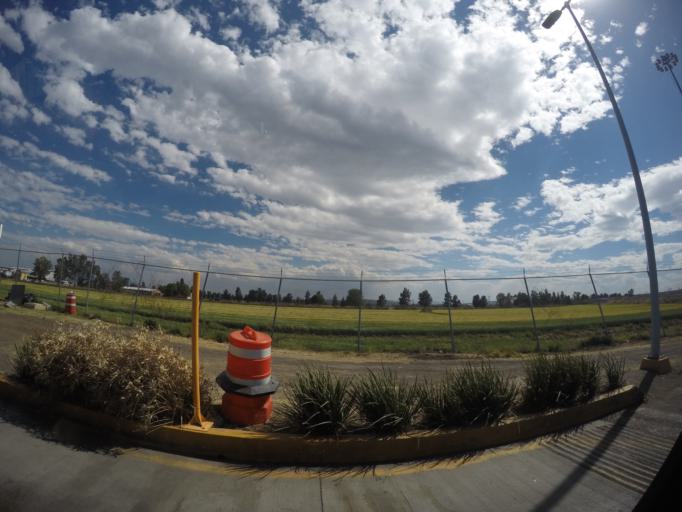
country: MX
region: Guanajuato
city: Cerro Gordo
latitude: 20.5902
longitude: -101.1384
